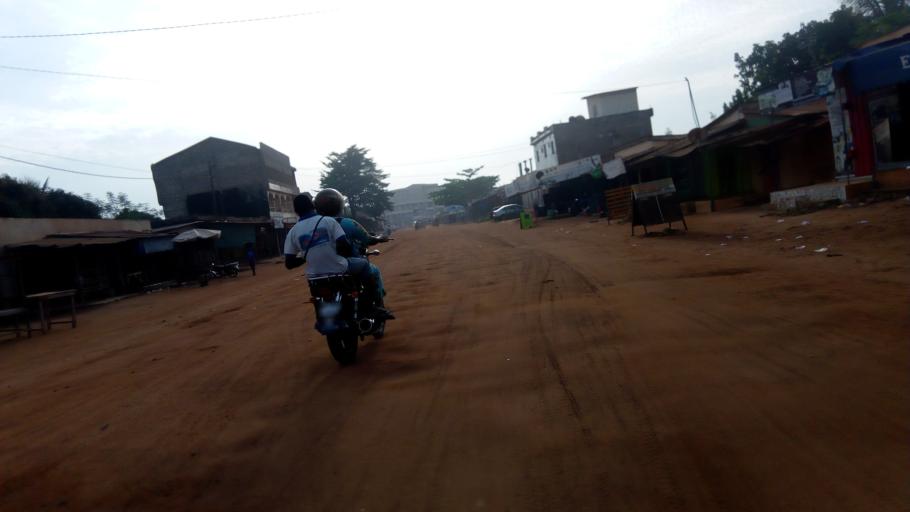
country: TG
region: Maritime
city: Lome
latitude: 6.1813
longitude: 1.1687
